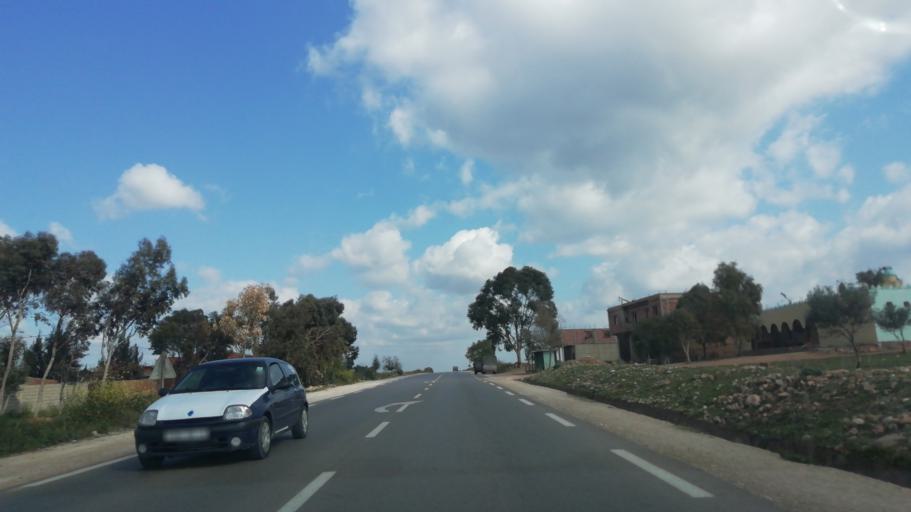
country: DZ
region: Relizane
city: Relizane
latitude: 35.7123
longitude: 0.2768
